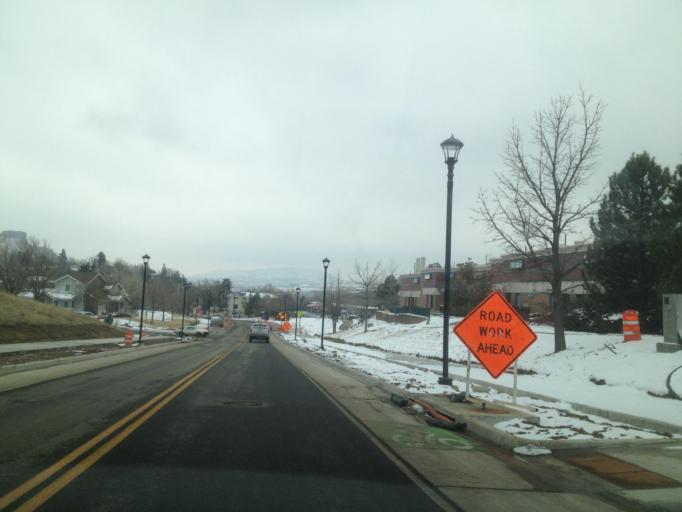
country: US
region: Colorado
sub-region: Jefferson County
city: Golden
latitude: 39.7671
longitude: -105.2329
